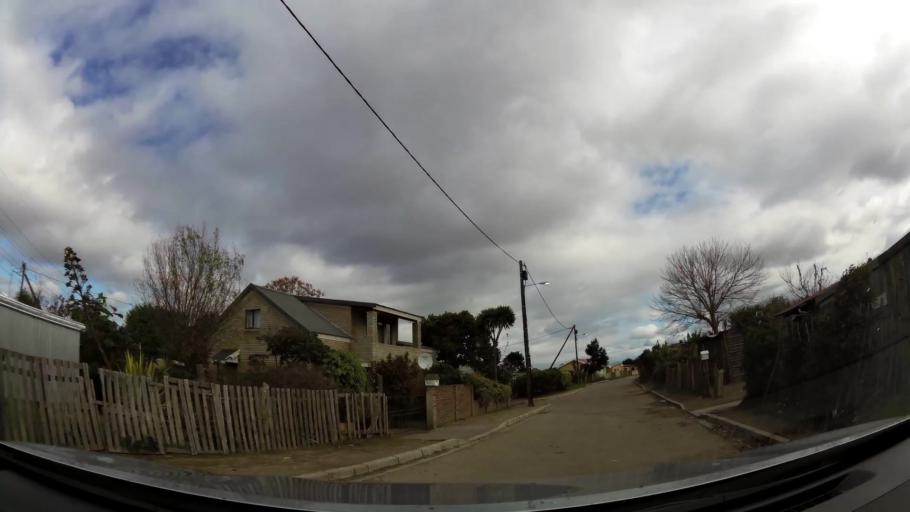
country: ZA
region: Western Cape
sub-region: Eden District Municipality
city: George
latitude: -33.9800
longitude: 22.4900
